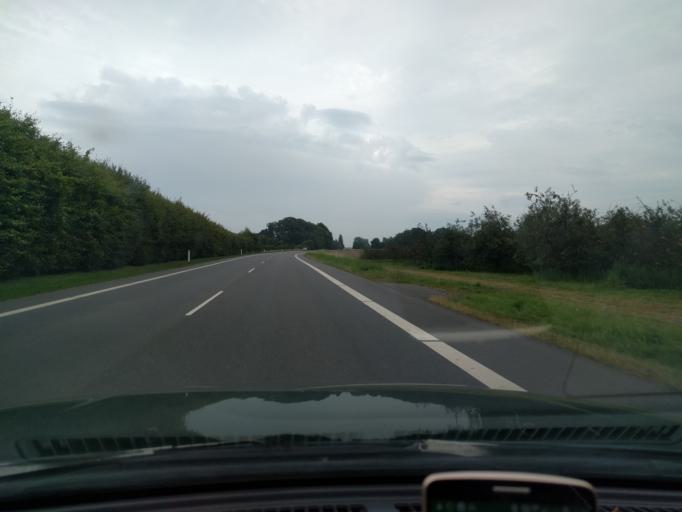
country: DK
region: Zealand
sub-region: Slagelse Kommune
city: Skaelskor
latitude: 55.2529
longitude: 11.3429
